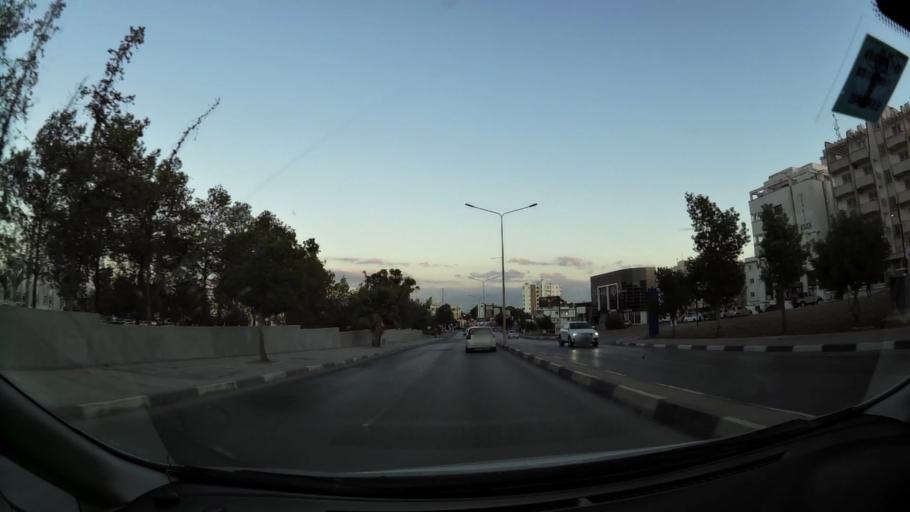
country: CY
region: Lefkosia
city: Nicosia
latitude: 35.2057
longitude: 33.3291
